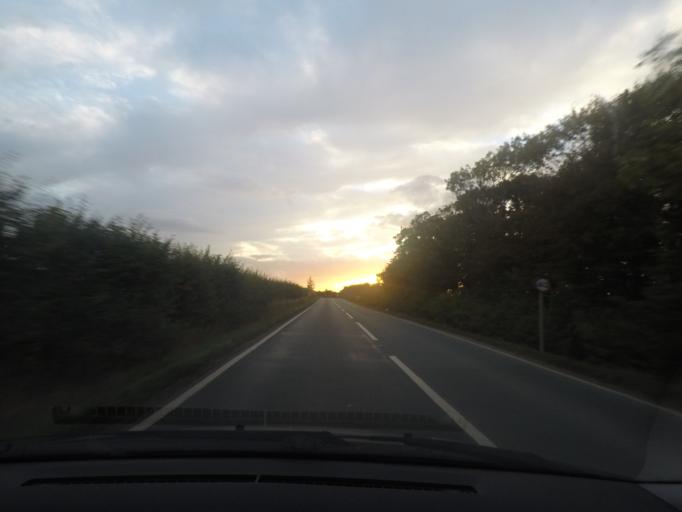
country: GB
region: England
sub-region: North Lincolnshire
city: Croxton
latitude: 53.5853
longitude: -0.3580
